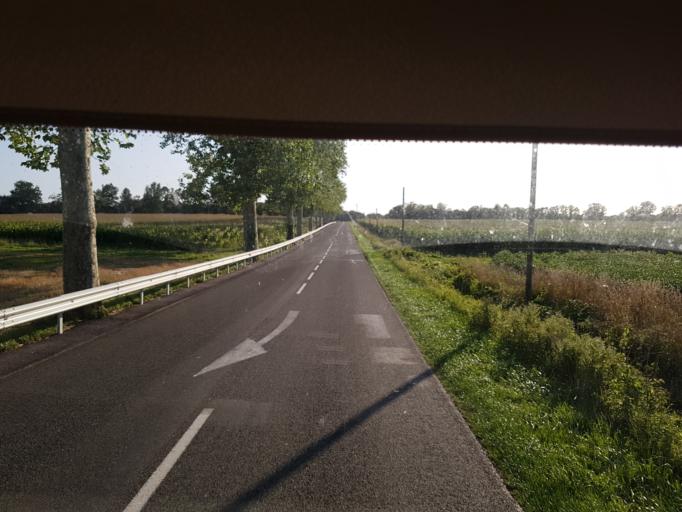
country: FR
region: Rhone-Alpes
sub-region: Departement de l'Ain
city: Chalamont
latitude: 45.9874
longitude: 5.1187
